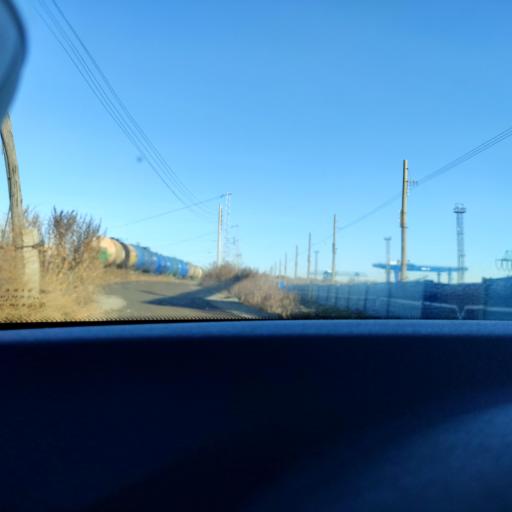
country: RU
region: Samara
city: Samara
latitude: 53.2040
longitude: 50.2495
